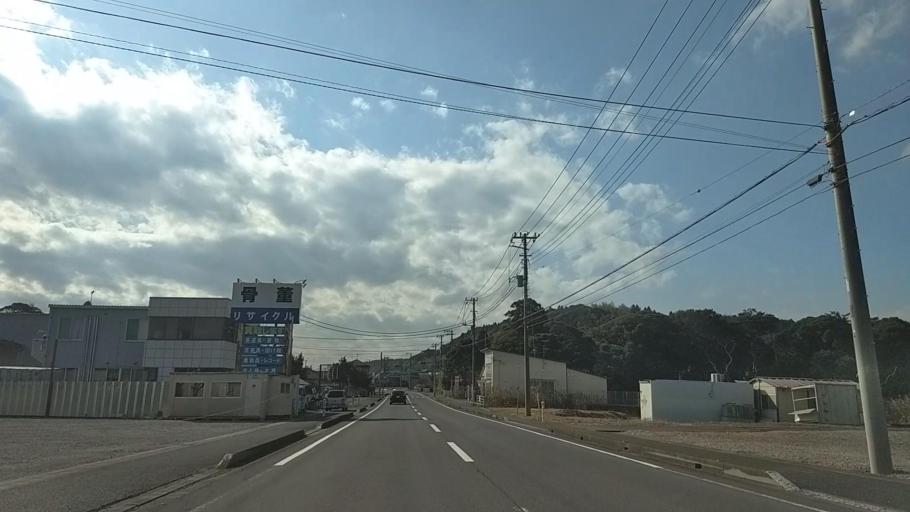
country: JP
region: Chiba
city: Naruto
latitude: 35.6250
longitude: 140.4419
